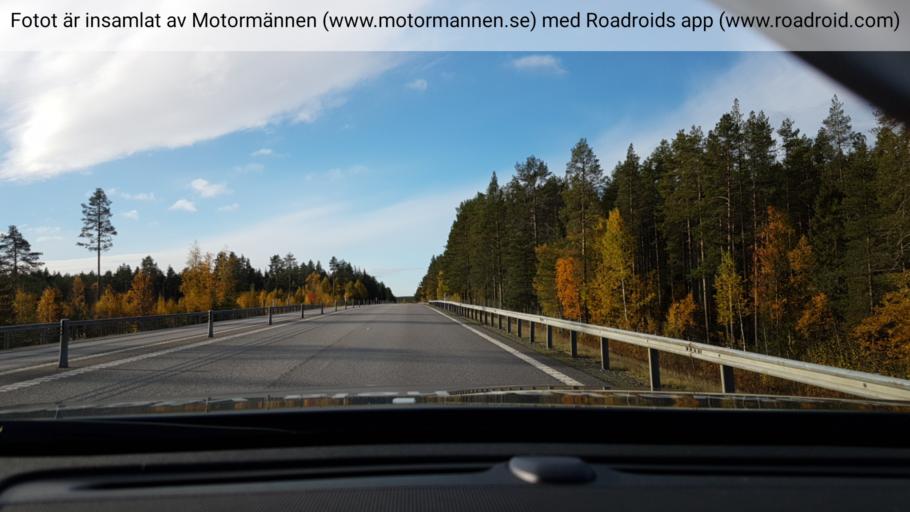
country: SE
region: Vaesterbotten
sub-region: Skelleftea Kommun
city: Byske
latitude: 65.0224
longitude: 21.3252
